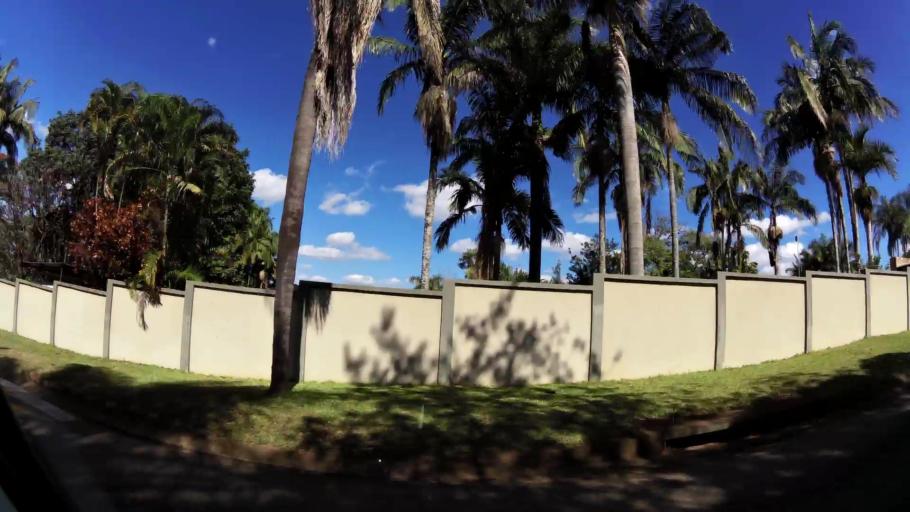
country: ZA
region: Limpopo
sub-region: Mopani District Municipality
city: Tzaneen
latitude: -23.8271
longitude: 30.1476
